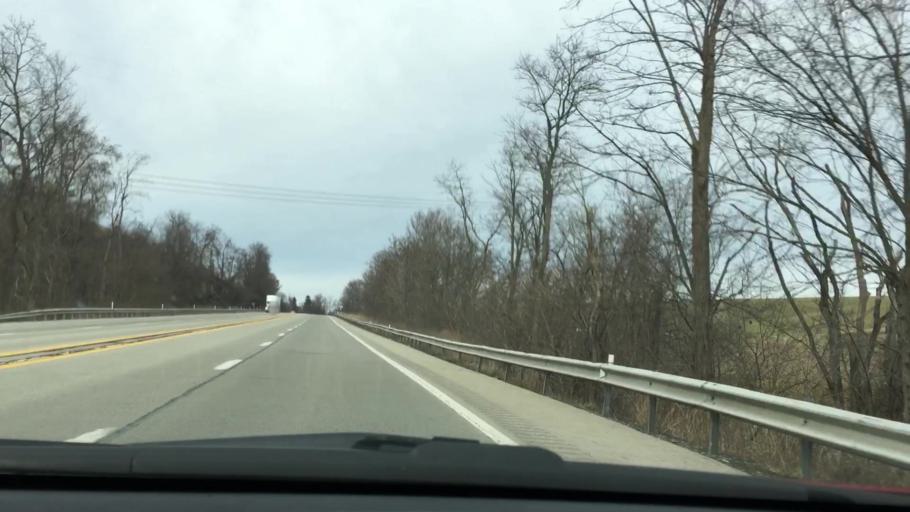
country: US
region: Pennsylvania
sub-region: Fayette County
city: Perryopolis
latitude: 40.0408
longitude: -79.7707
